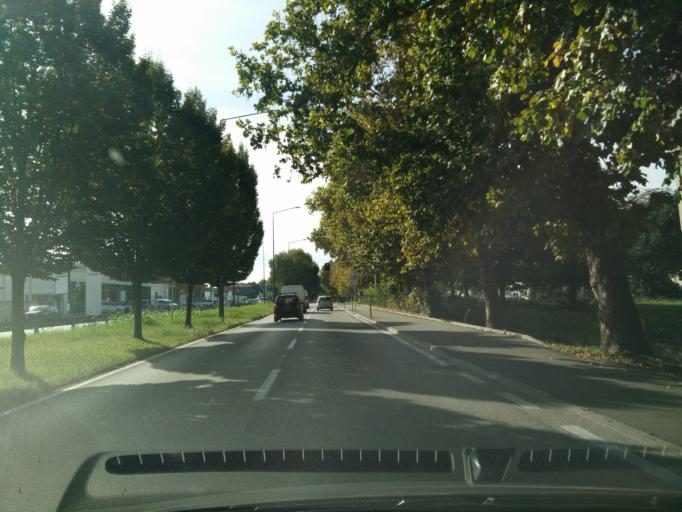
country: IT
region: Veneto
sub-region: Provincia di Venezia
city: Mestre
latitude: 45.4687
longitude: 12.2274
